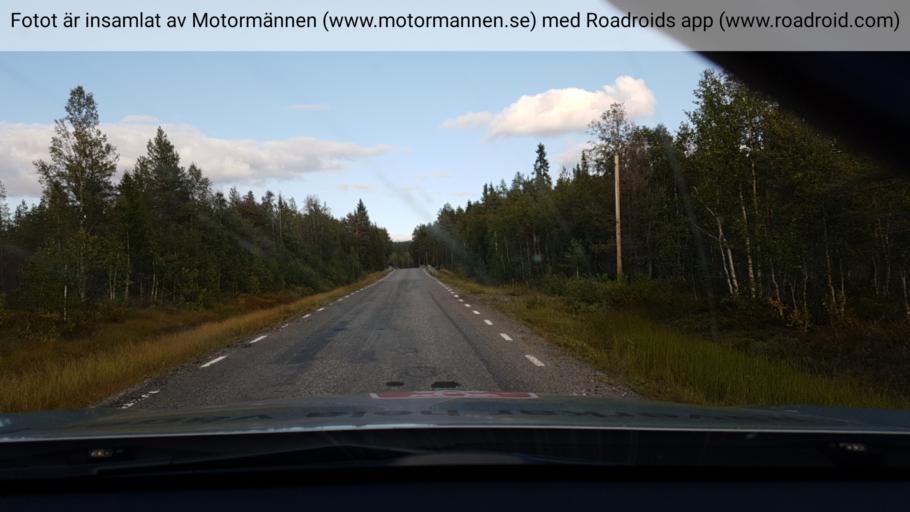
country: SE
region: Vaesterbotten
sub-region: Norsjo Kommun
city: Norsjoe
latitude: 64.9555
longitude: 19.2808
